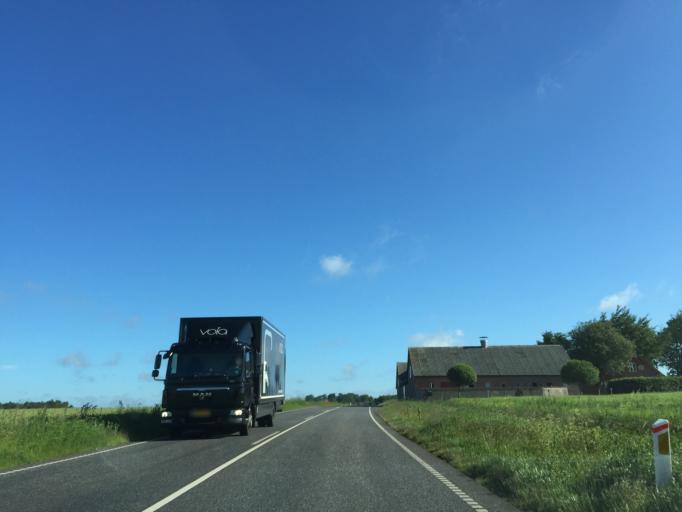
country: DK
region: Central Jutland
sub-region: Viborg Kommune
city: Bjerringbro
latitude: 56.3433
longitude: 9.6801
